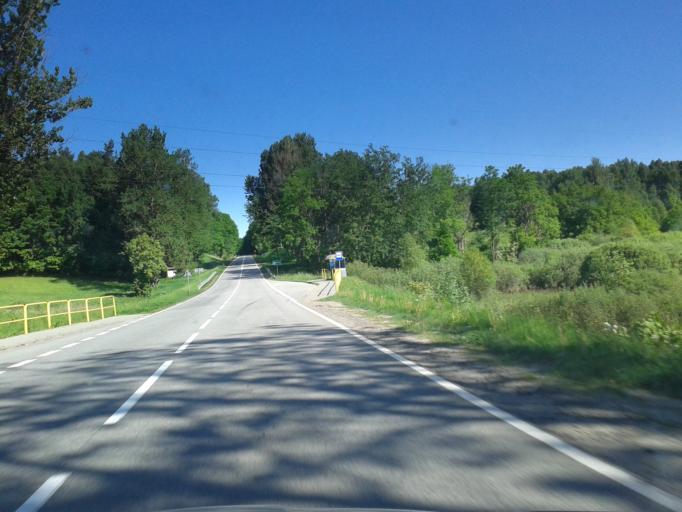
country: PL
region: West Pomeranian Voivodeship
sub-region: Powiat koszalinski
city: Bobolice
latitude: 53.9138
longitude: 16.6075
